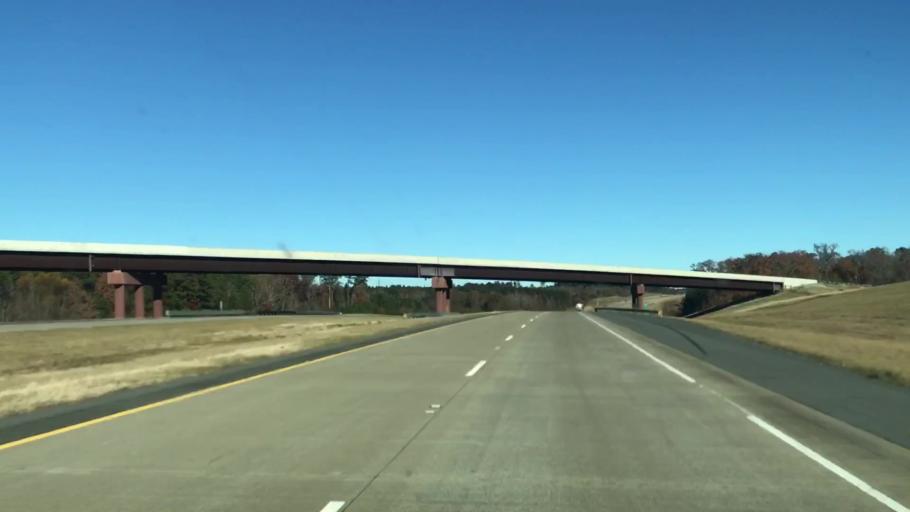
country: US
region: Louisiana
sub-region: Caddo Parish
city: Vivian
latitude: 32.9773
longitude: -93.9093
